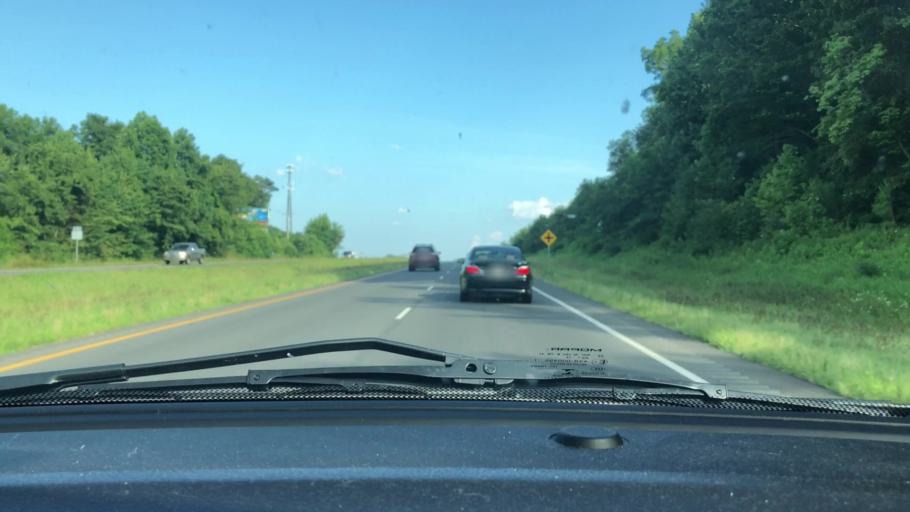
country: US
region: North Carolina
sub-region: Chatham County
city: Siler City
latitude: 35.6552
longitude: -79.3955
